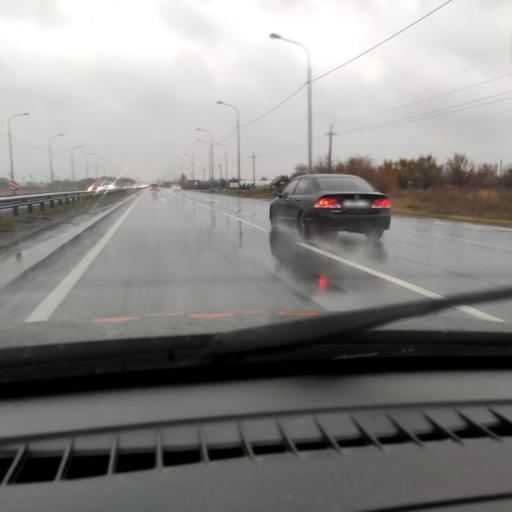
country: RU
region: Samara
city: Tol'yatti
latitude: 53.5751
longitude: 49.4411
